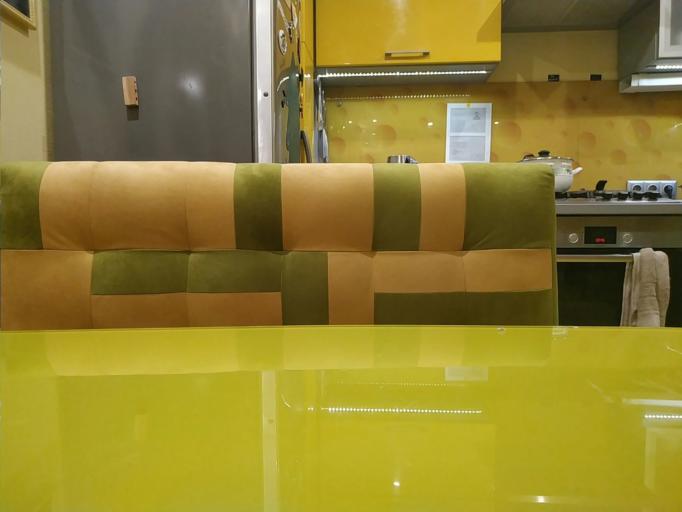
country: RU
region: Murmansk
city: Alakurtti
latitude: 66.2652
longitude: 30.2604
